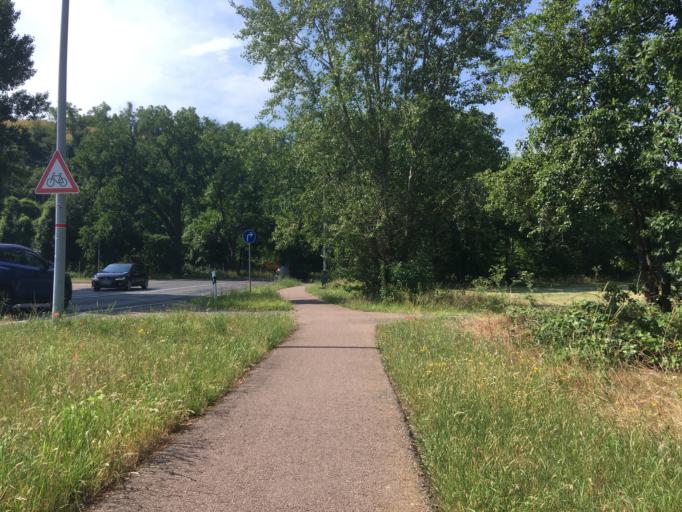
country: DE
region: Saxony-Anhalt
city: Dessau
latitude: 51.8086
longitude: 12.2100
